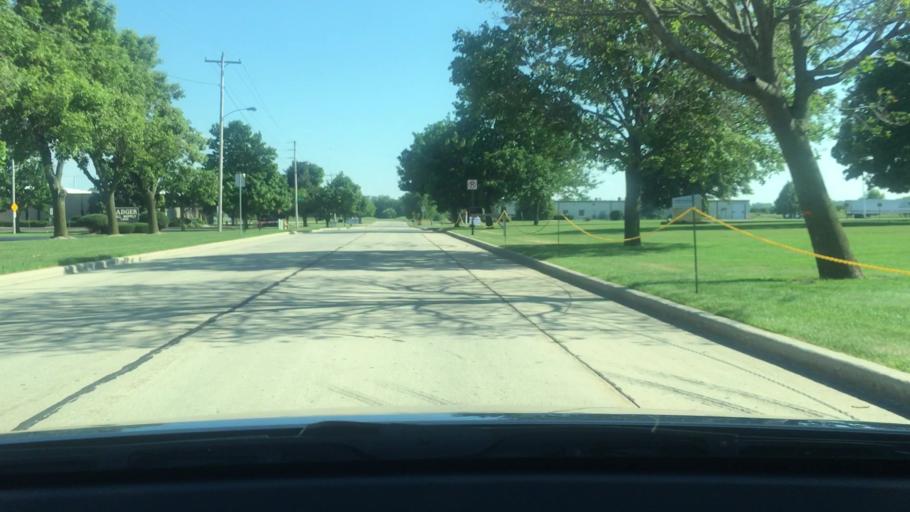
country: US
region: Wisconsin
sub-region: Winnebago County
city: Oshkosh
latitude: 43.9789
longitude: -88.5506
